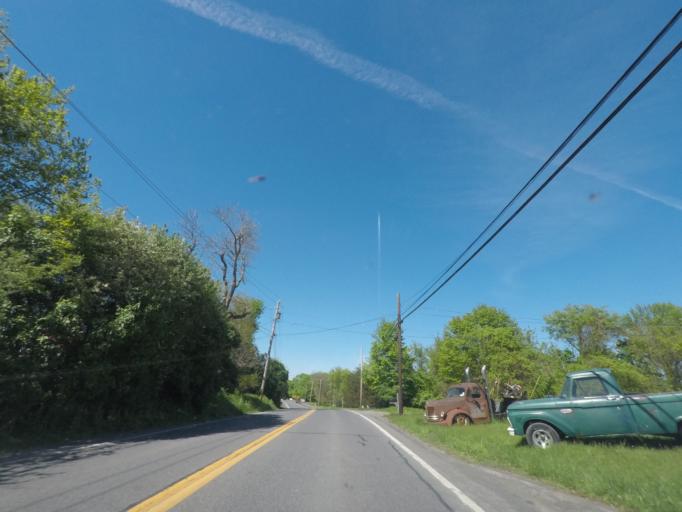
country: US
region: New York
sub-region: Ulster County
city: Saugerties
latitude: 42.0961
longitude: -73.9393
